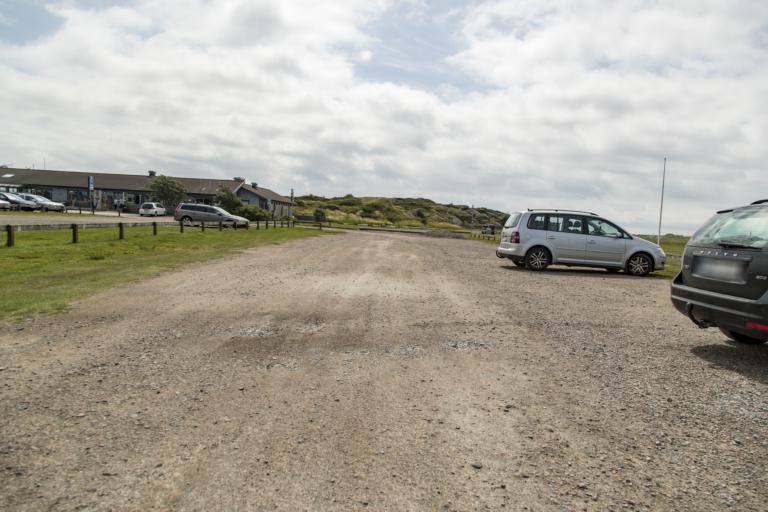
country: SE
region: Halland
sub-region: Varbergs Kommun
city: Varberg
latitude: 57.1138
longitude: 12.2252
